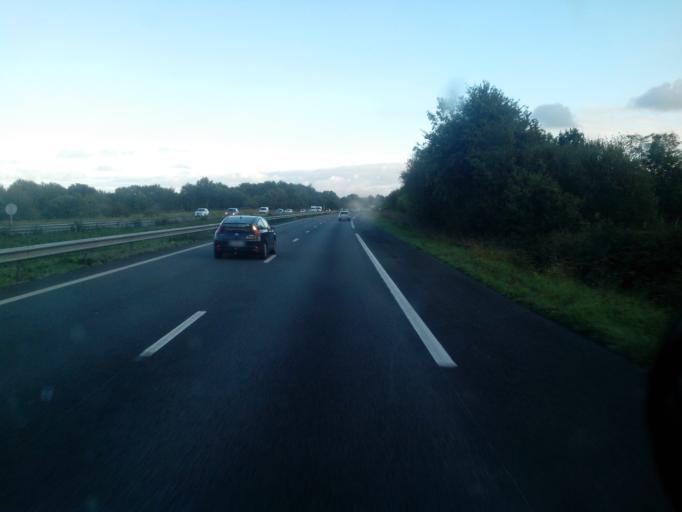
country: FR
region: Pays de la Loire
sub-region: Departement de la Loire-Atlantique
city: Le Temple-de-Bretagne
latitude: 47.3290
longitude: -1.7839
